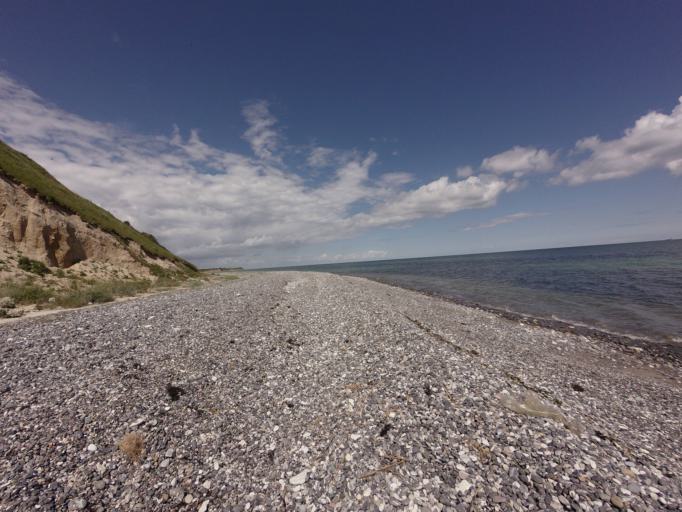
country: DK
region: Central Jutland
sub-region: Norddjurs Kommune
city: Grenaa
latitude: 56.5172
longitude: 10.8621
